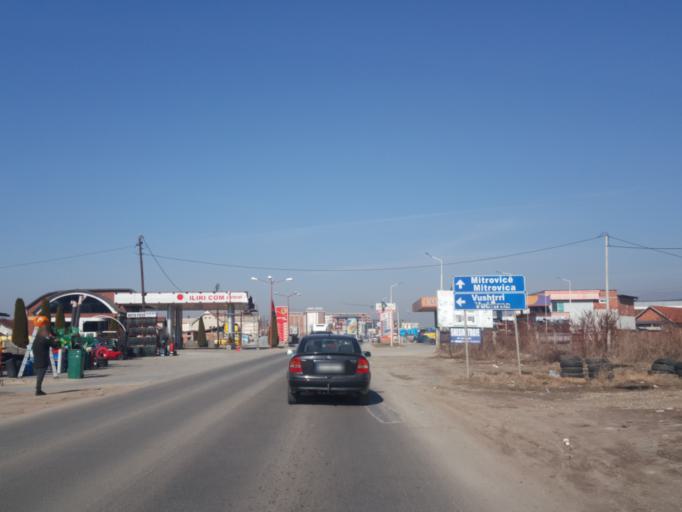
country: XK
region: Mitrovica
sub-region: Vushtrri
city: Vushtrri
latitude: 42.8130
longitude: 20.9847
